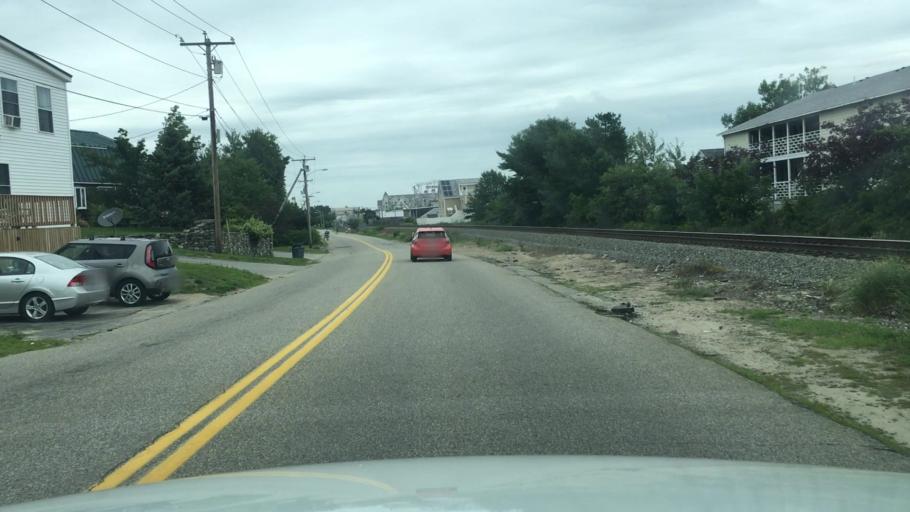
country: US
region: Maine
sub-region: York County
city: Old Orchard Beach
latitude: 43.5104
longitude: -70.3795
